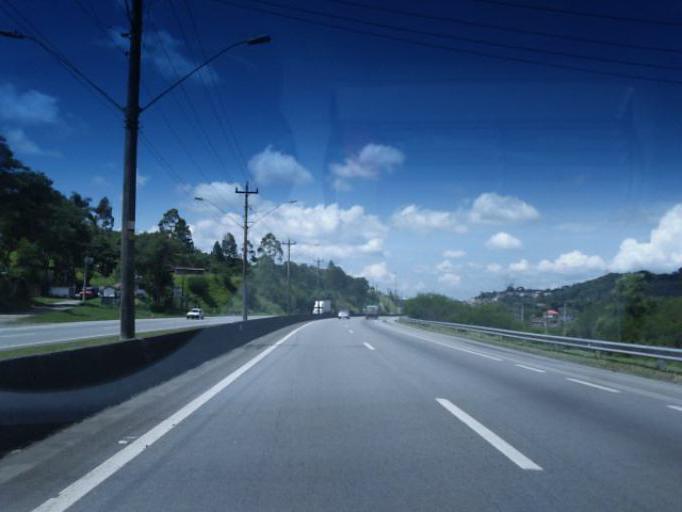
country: BR
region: Sao Paulo
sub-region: Sao Lourenco Da Serra
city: Sao Lourenco da Serra
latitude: -23.8782
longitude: -46.9687
